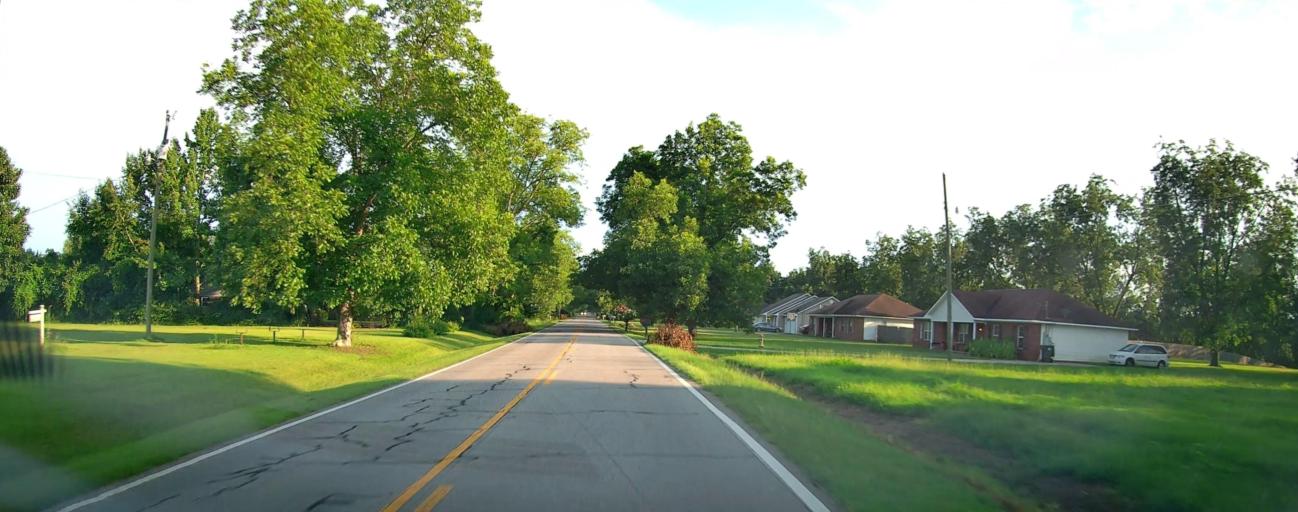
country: US
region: Georgia
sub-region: Peach County
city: Fort Valley
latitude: 32.5867
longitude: -83.8739
